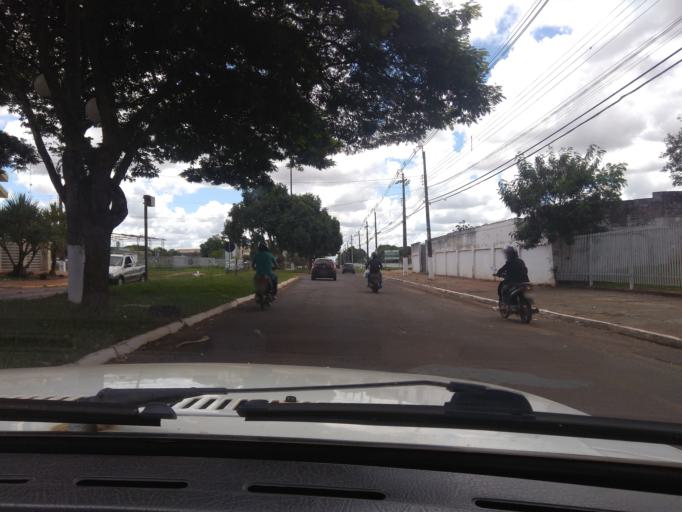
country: BR
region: Mato Grosso do Sul
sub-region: Ponta Pora
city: Ponta Pora
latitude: -22.5250
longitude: -55.7234
